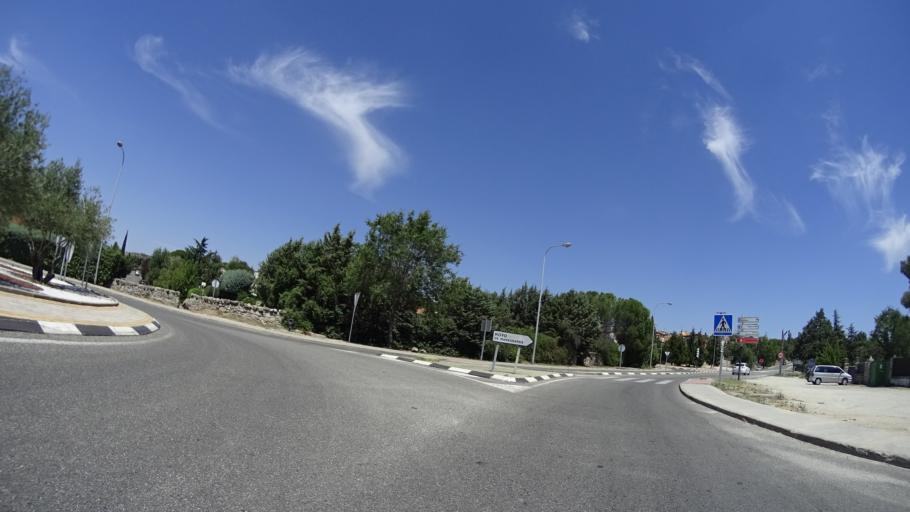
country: ES
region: Madrid
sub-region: Provincia de Madrid
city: Torrelodones
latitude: 40.5779
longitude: -3.9223
